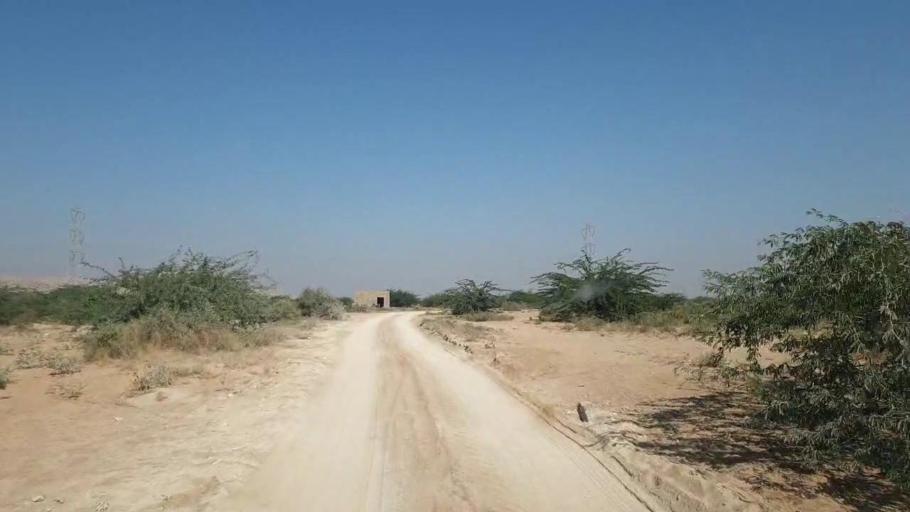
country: PK
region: Sindh
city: Gharo
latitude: 25.1927
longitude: 67.7412
